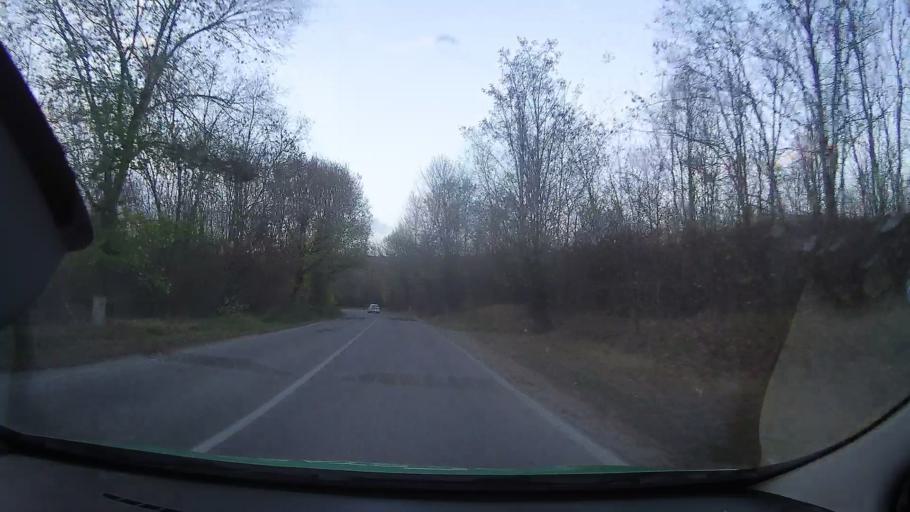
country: RO
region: Constanta
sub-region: Comuna Baneasa
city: Baneasa
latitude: 44.0857
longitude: 27.6662
